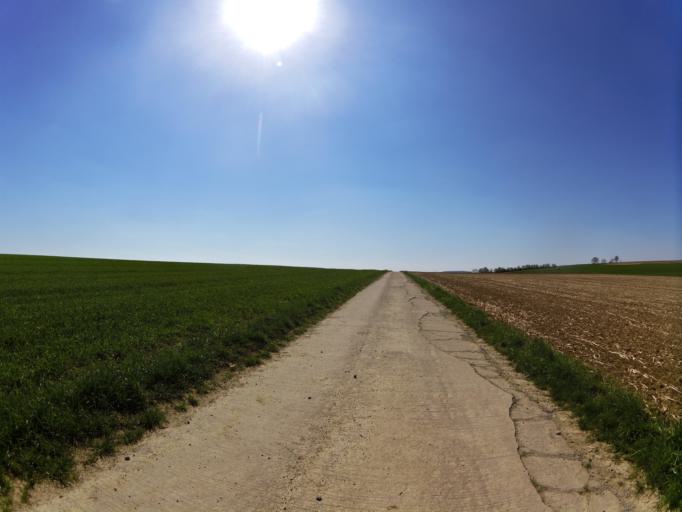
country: DE
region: Bavaria
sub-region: Regierungsbezirk Unterfranken
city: Winterhausen
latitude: 49.6826
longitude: 10.0086
